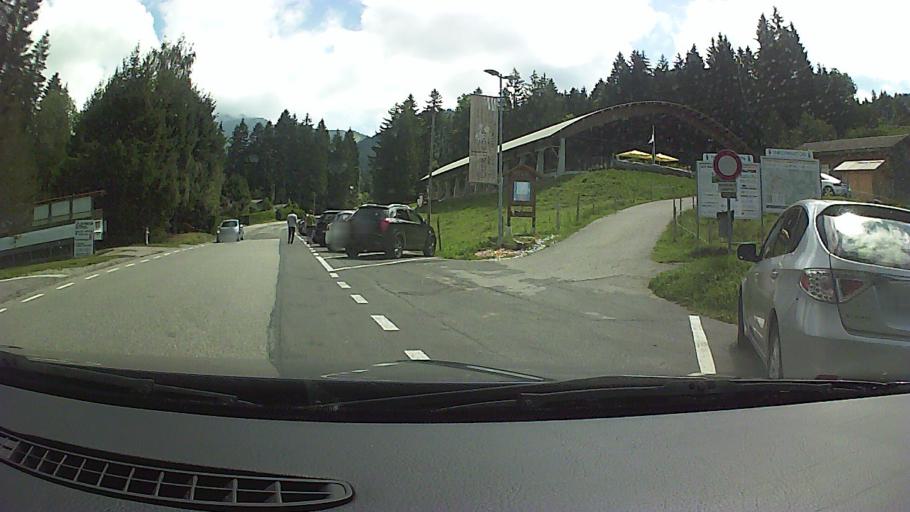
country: CH
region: Fribourg
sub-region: Veveyse District
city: Chatel-Saint-Denis
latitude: 46.5215
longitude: 6.9505
